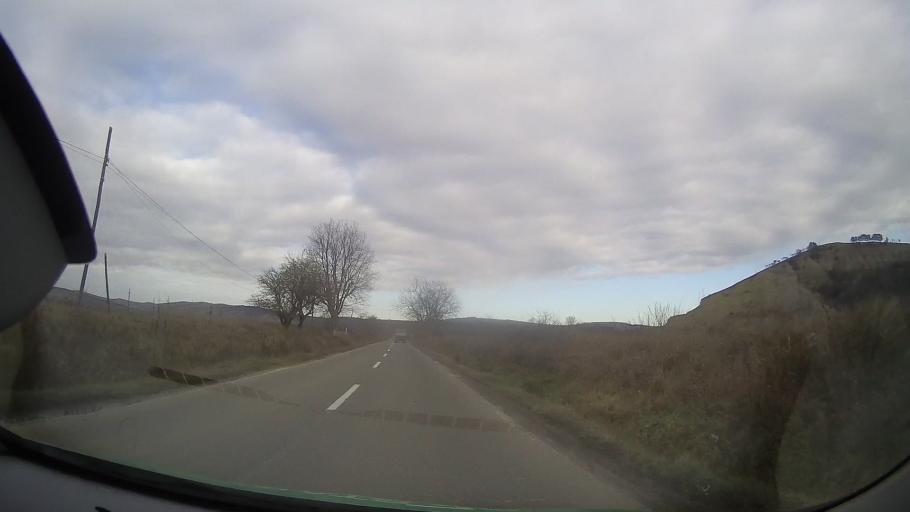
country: RO
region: Mures
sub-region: Comuna Iernut
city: Iernut
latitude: 46.4645
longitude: 24.2182
